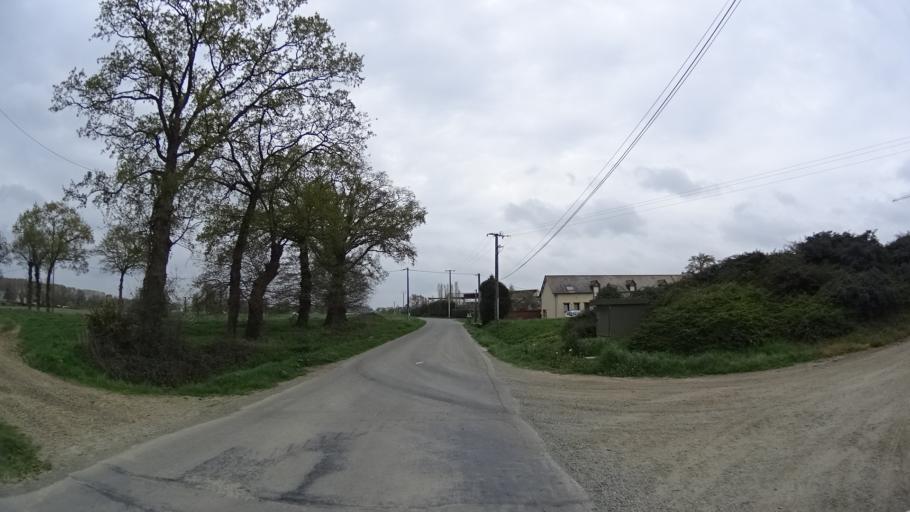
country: FR
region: Brittany
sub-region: Departement d'Ille-et-Vilaine
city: Cintre
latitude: 48.1114
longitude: -1.8721
